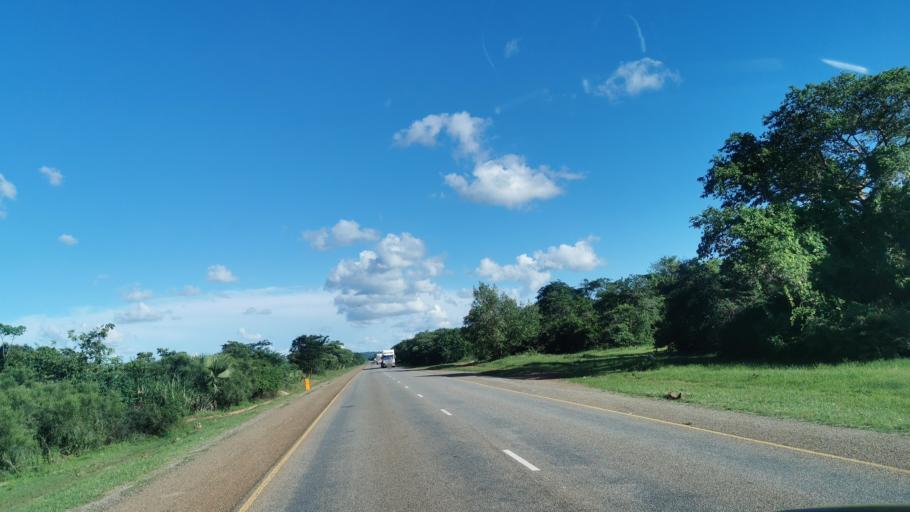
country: TZ
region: Geita
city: Masumbwe
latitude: -3.7192
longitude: 32.2950
